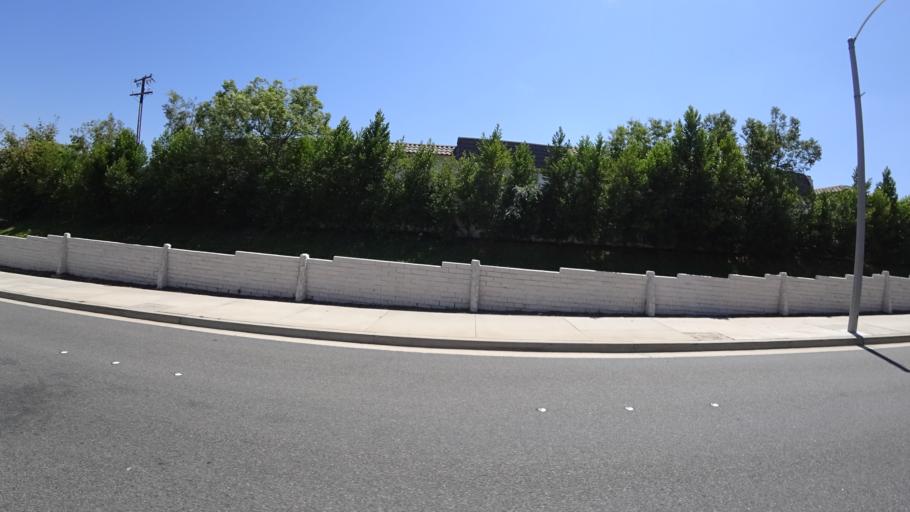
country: US
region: California
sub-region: Los Angeles County
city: Santa Clarita
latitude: 34.3786
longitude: -118.5602
